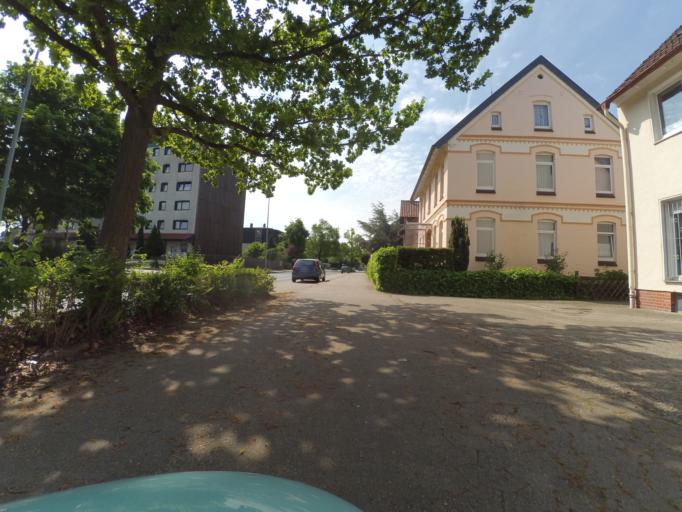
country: DE
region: Lower Saxony
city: Sehnde
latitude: 52.3129
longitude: 9.9637
